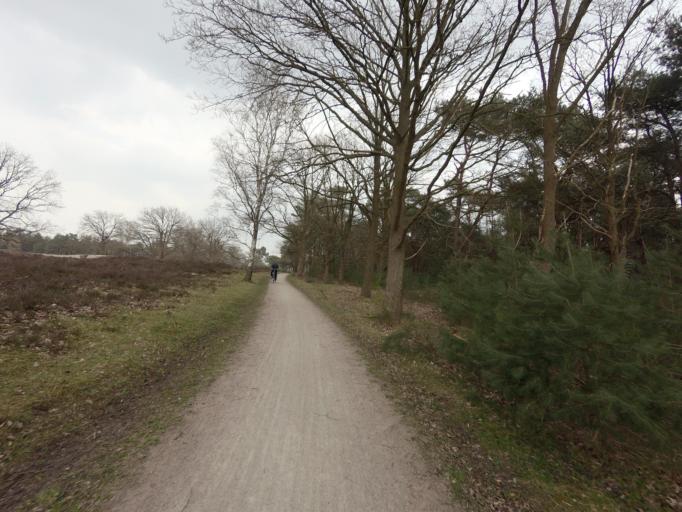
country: NL
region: North Holland
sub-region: Gemeente Huizen
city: Huizen
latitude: 52.2963
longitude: 5.2074
